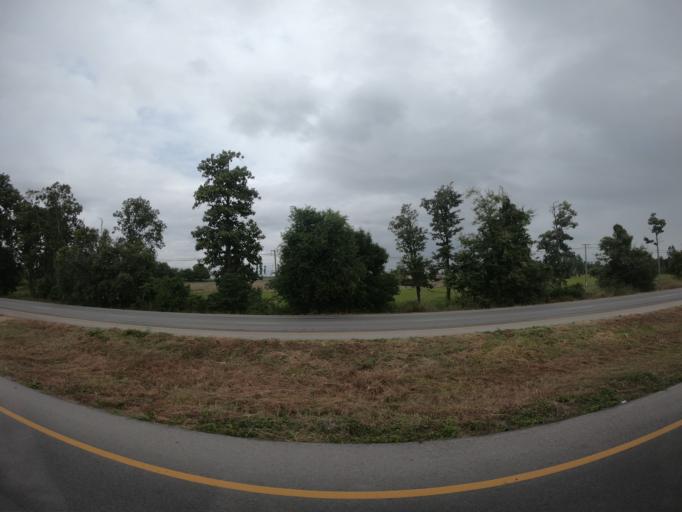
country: TH
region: Maha Sarakham
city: Kut Rang
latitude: 16.0498
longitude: 102.9444
